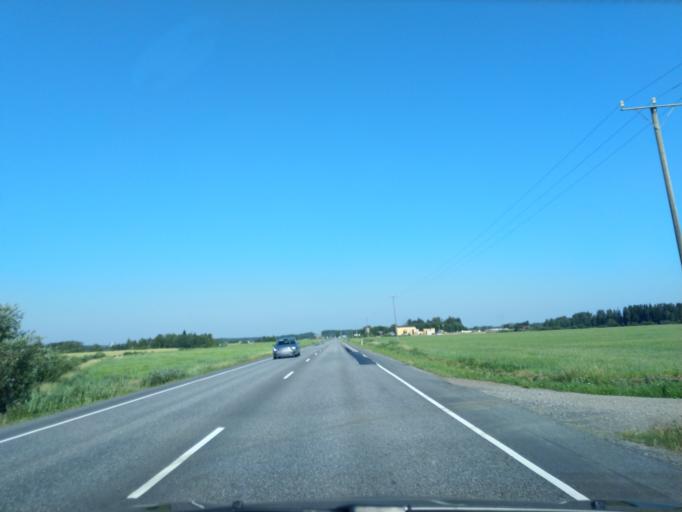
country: FI
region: Pirkanmaa
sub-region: Lounais-Pirkanmaa
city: Punkalaidun
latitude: 61.0360
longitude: 23.0087
